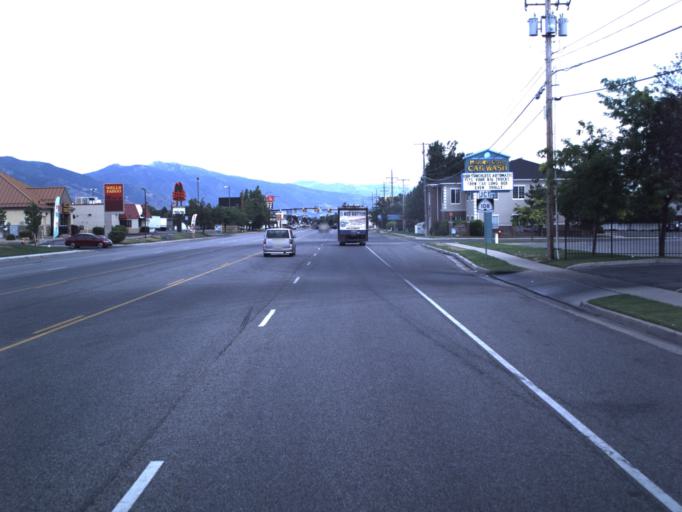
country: US
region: Utah
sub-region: Davis County
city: Clearfield
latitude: 41.0913
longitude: -112.0033
